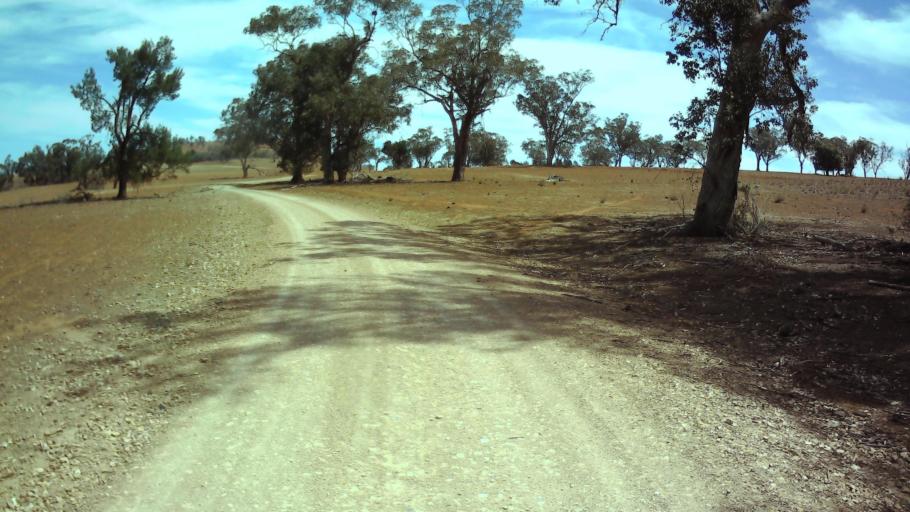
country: AU
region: New South Wales
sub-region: Weddin
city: Grenfell
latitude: -33.7447
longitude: 148.1723
